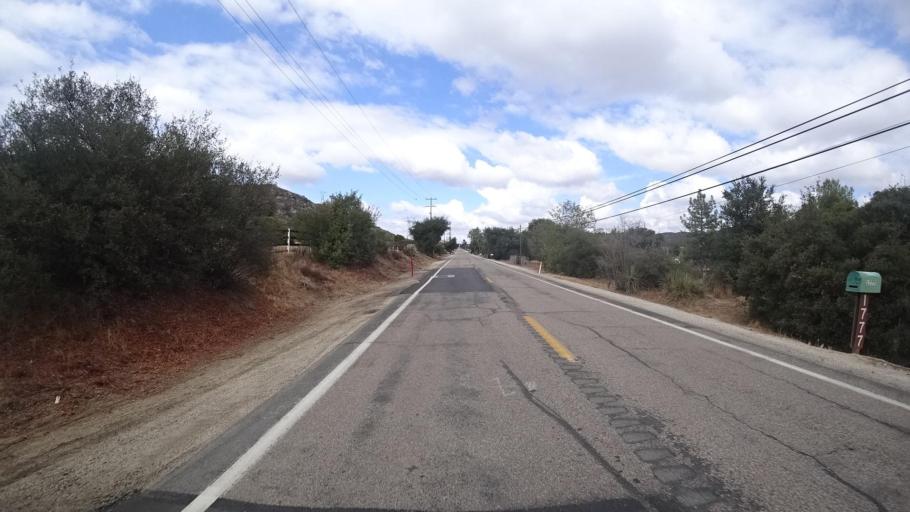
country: US
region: California
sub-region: San Diego County
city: Campo
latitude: 32.6503
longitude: -116.4874
